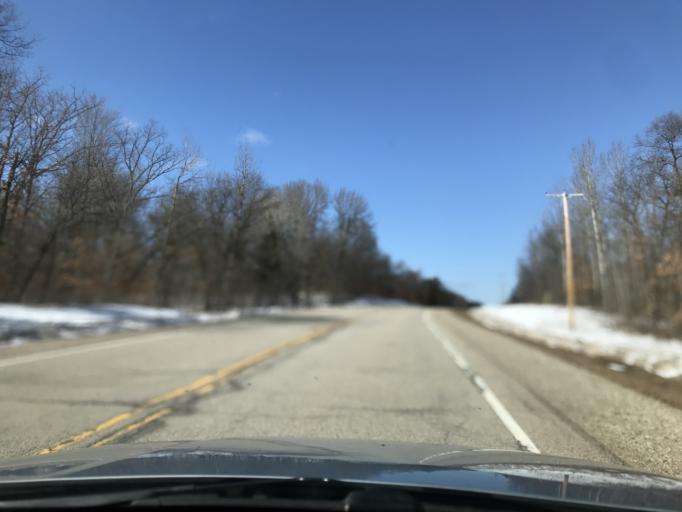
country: US
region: Wisconsin
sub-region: Marinette County
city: Niagara
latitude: 45.3398
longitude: -88.1013
